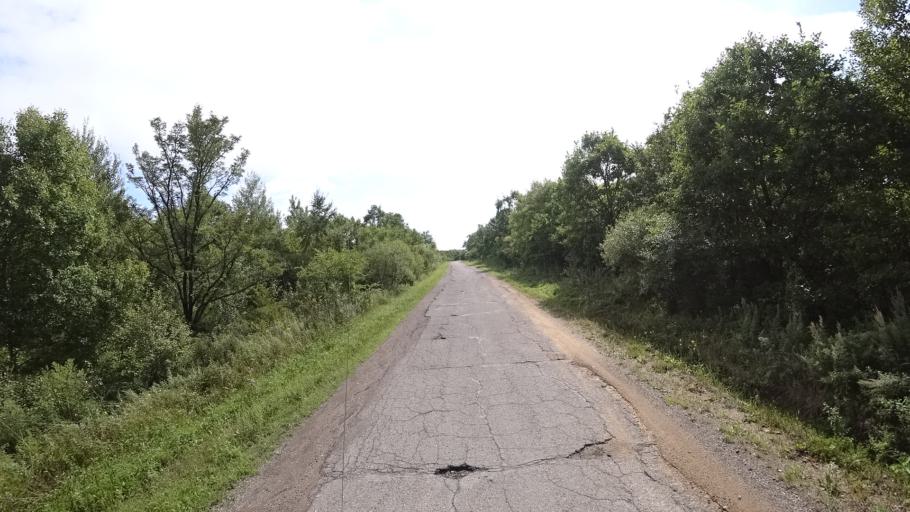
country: RU
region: Primorskiy
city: Lyalichi
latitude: 44.1480
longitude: 132.3902
